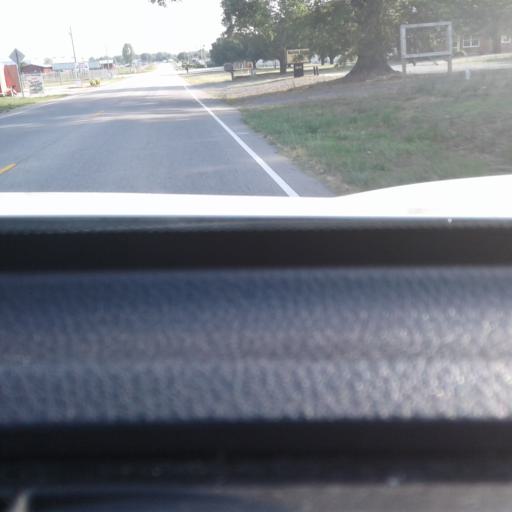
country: US
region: North Carolina
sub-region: Harnett County
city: Dunn
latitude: 35.3342
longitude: -78.5913
